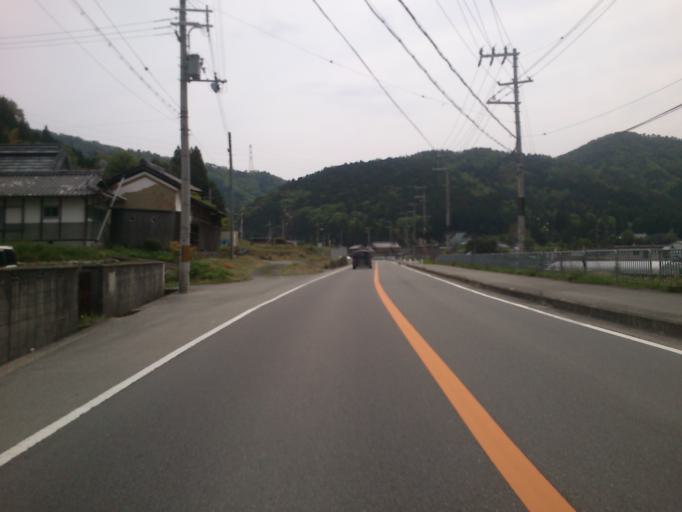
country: JP
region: Kyoto
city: Kameoka
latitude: 34.9773
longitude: 135.5429
